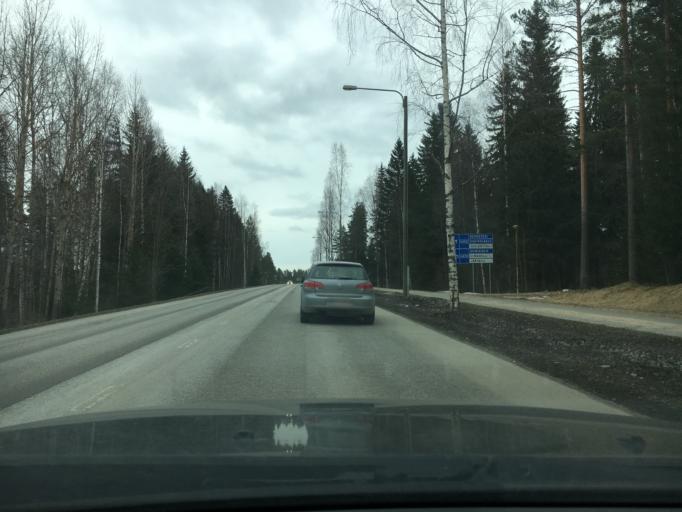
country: FI
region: Central Finland
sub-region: AEaenekoski
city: Suolahti
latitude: 62.5595
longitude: 25.8669
